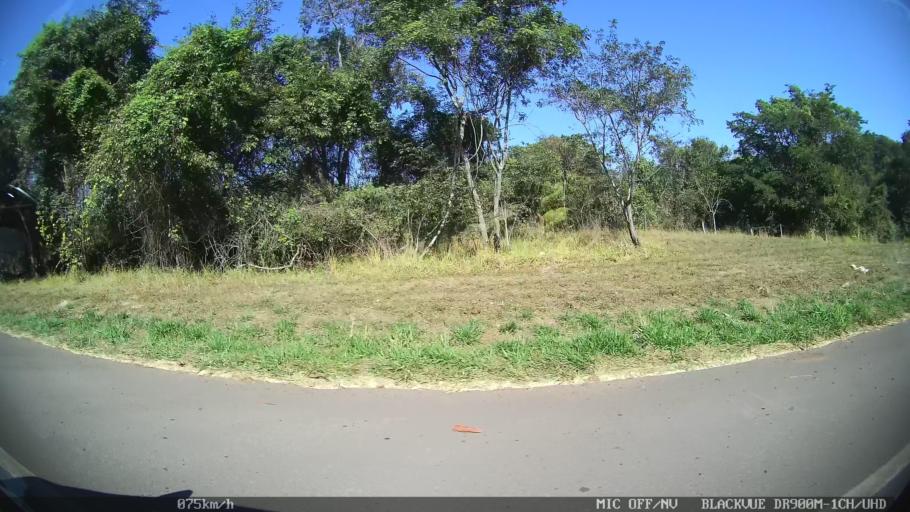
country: BR
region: Sao Paulo
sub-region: Batatais
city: Batatais
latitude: -20.9123
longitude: -47.5891
